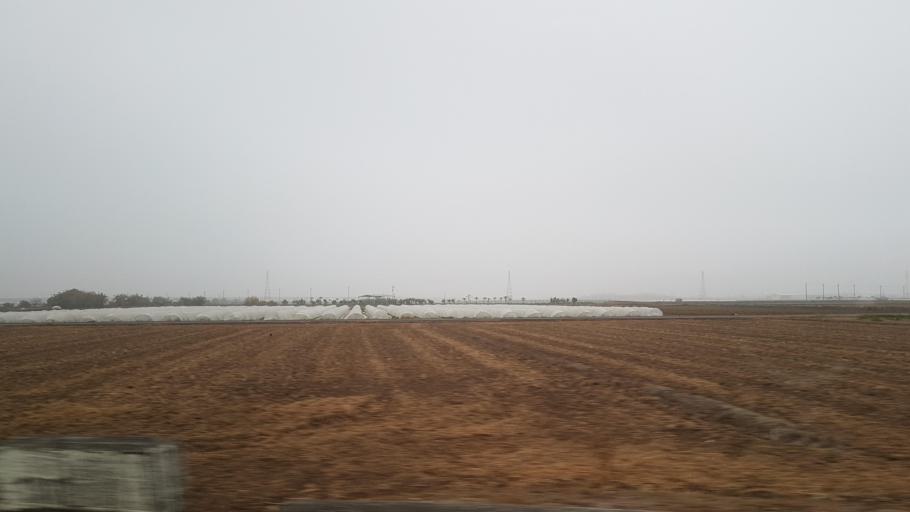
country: TW
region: Taiwan
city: Xinying
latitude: 23.3434
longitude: 120.3455
